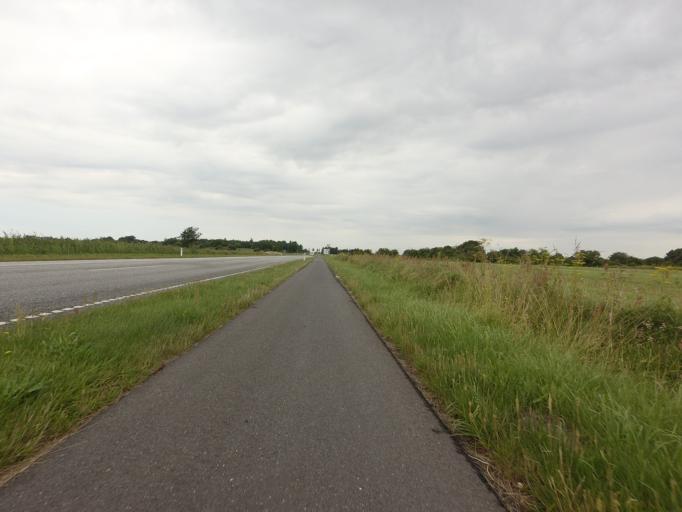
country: DK
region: North Denmark
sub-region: Alborg Kommune
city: Aalborg
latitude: 57.0810
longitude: 9.8902
